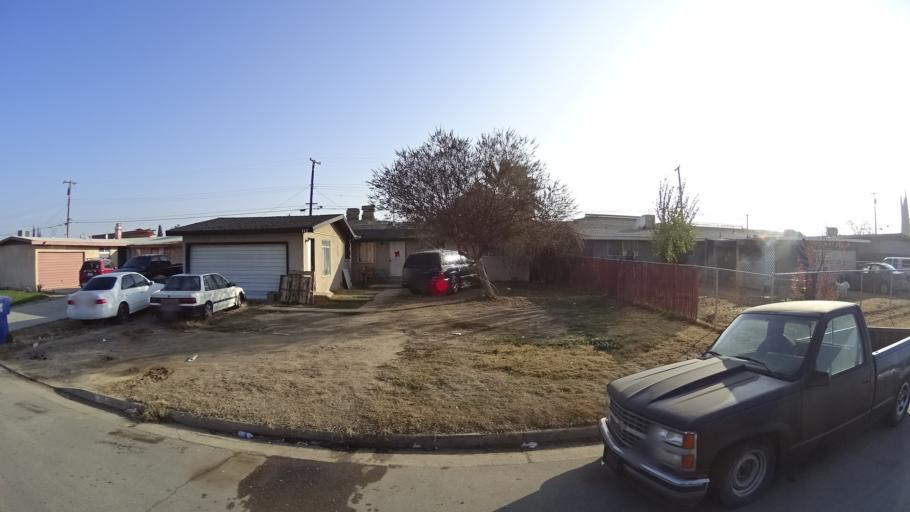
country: US
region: California
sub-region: Kern County
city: Bakersfield
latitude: 35.3560
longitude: -119.0509
